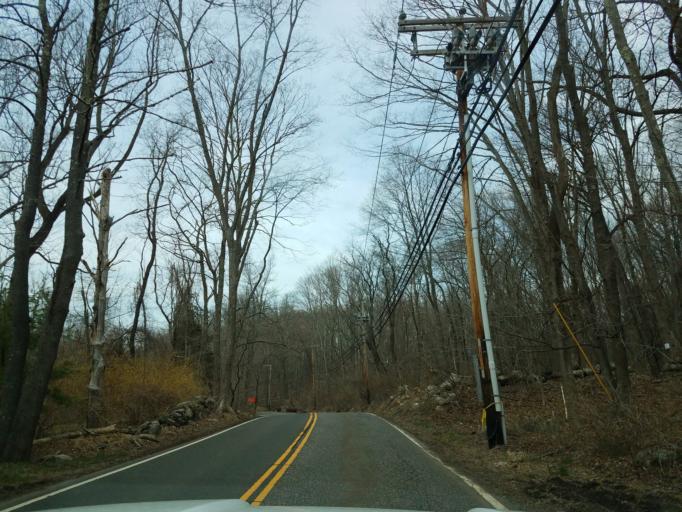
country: US
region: New York
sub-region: Westchester County
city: Armonk
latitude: 41.1046
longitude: -73.6522
